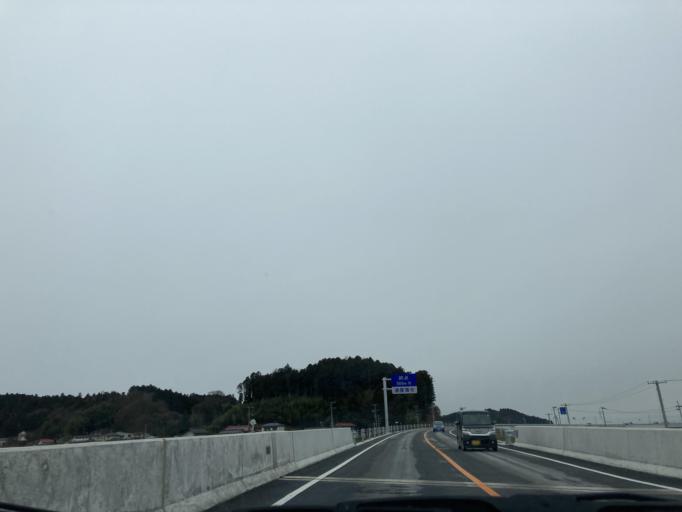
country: JP
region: Miyagi
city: Wakuya
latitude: 38.7026
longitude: 141.1835
